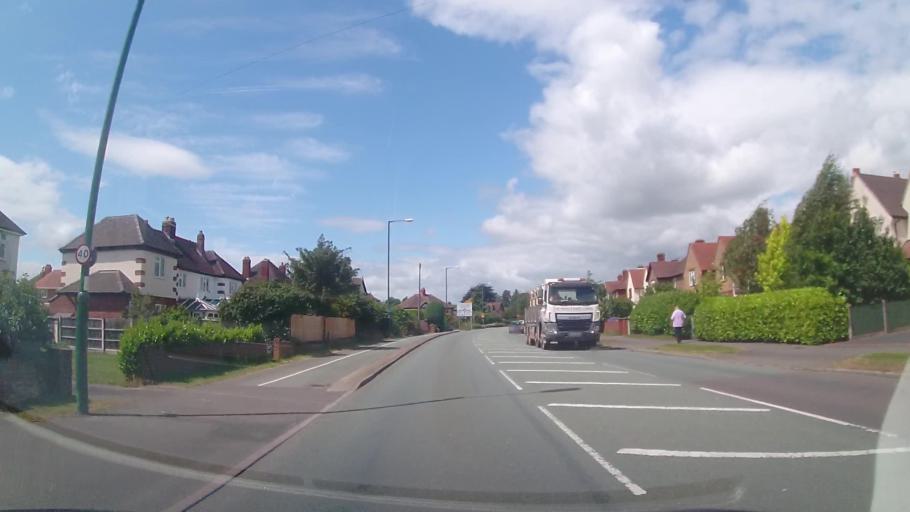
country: GB
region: England
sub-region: Shropshire
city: Shrewsbury
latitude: 52.7065
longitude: -2.7767
